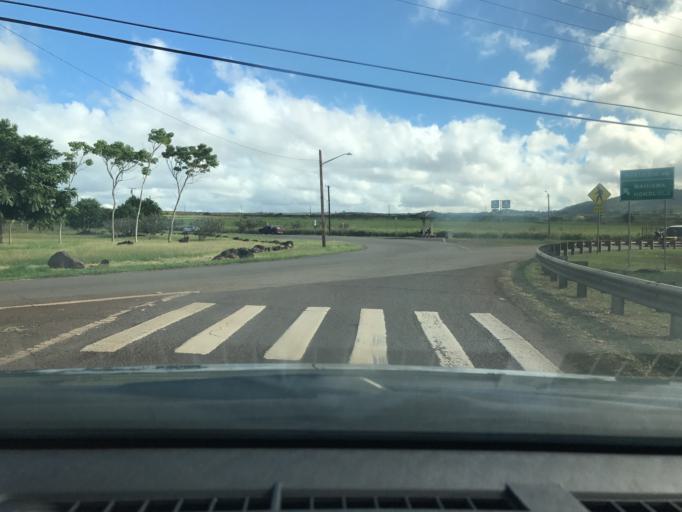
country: US
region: Hawaii
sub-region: Honolulu County
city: Hale'iwa
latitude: 21.5758
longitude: -158.1067
